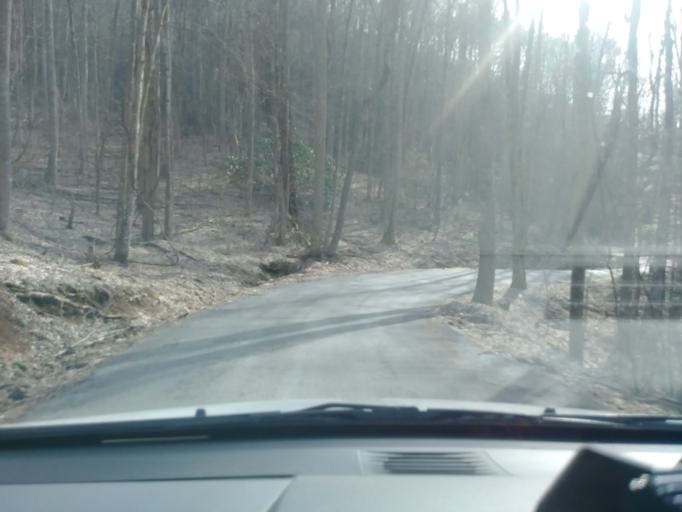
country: US
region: Tennessee
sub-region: Greene County
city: Tusculum
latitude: 36.0224
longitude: -82.7352
